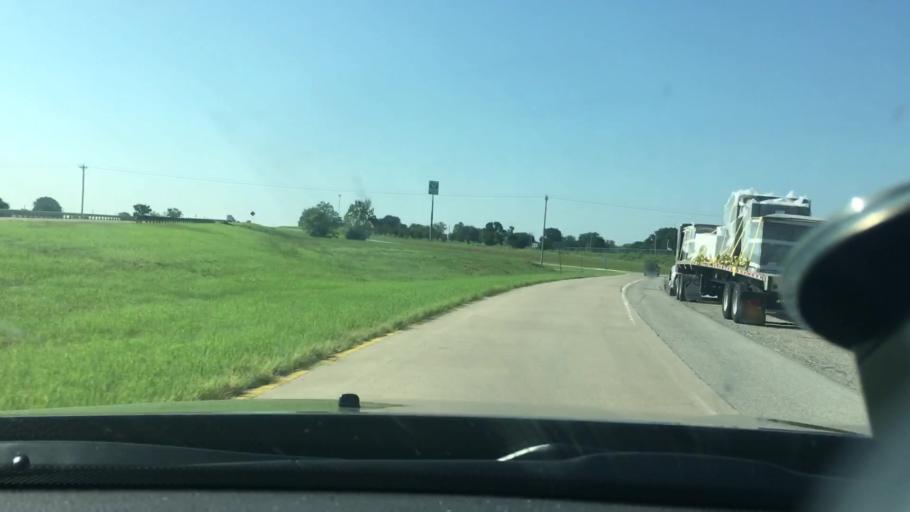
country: US
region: Oklahoma
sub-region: Love County
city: Marietta
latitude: 34.0290
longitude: -97.1495
